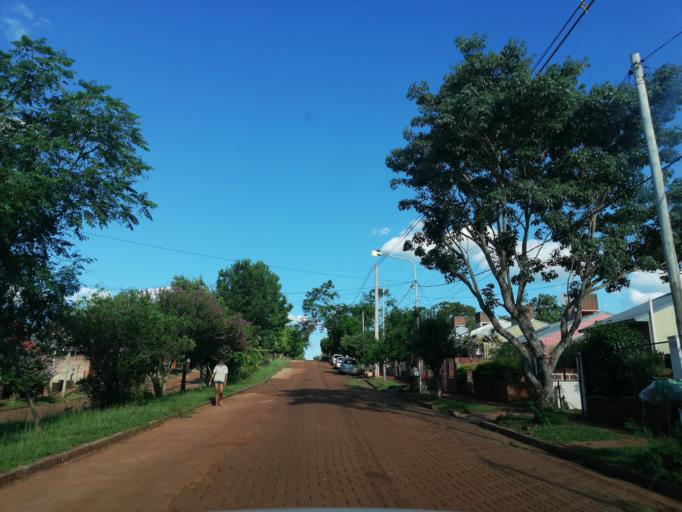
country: AR
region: Misiones
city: Garupa
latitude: -27.4661
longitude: -55.8778
